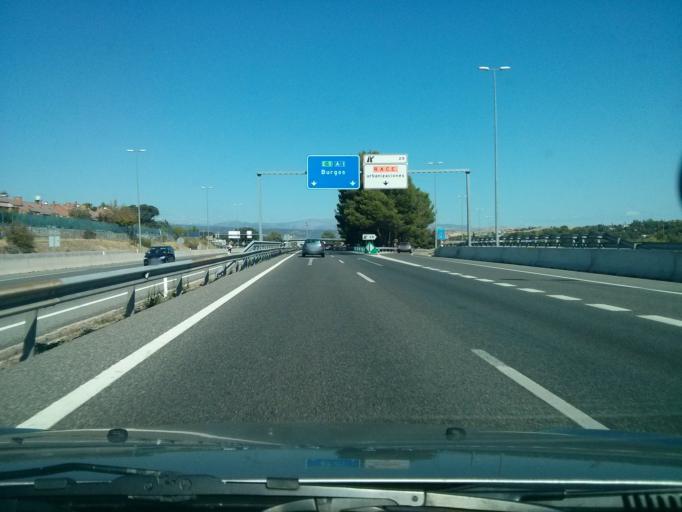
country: ES
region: Madrid
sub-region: Provincia de Madrid
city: San Agustin de Guadalix
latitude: 40.6232
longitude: -3.5857
